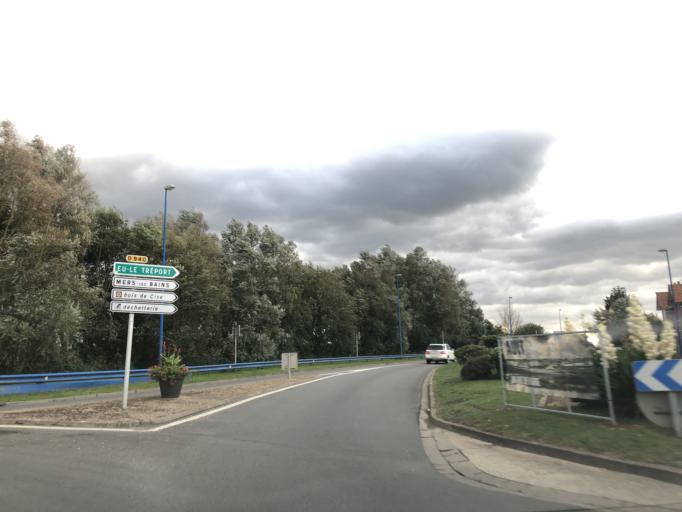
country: FR
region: Picardie
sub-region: Departement de la Somme
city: Ault
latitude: 50.0948
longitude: 1.4631
